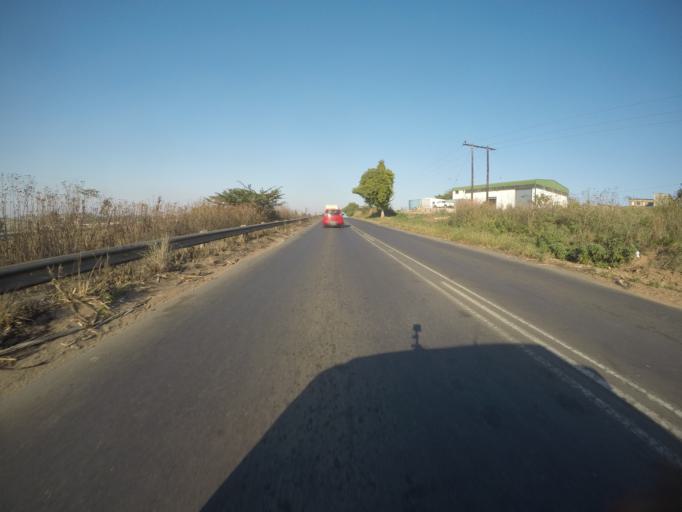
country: ZA
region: KwaZulu-Natal
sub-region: iLembe District Municipality
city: Stanger
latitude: -29.4083
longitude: 31.2473
